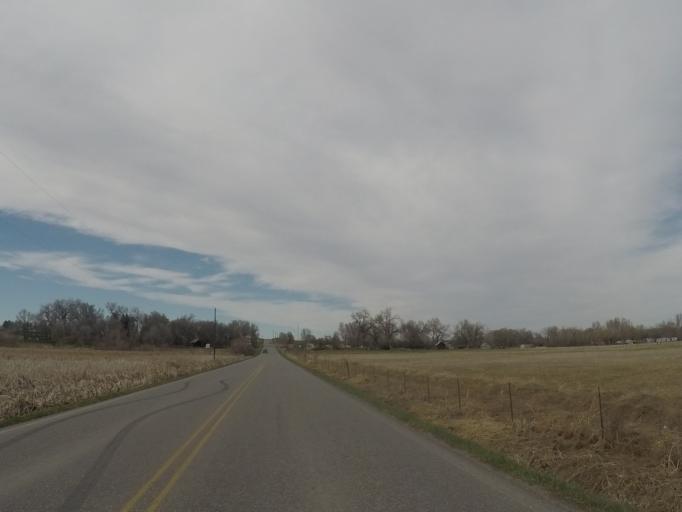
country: US
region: Montana
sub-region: Yellowstone County
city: Laurel
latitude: 45.7074
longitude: -108.6587
